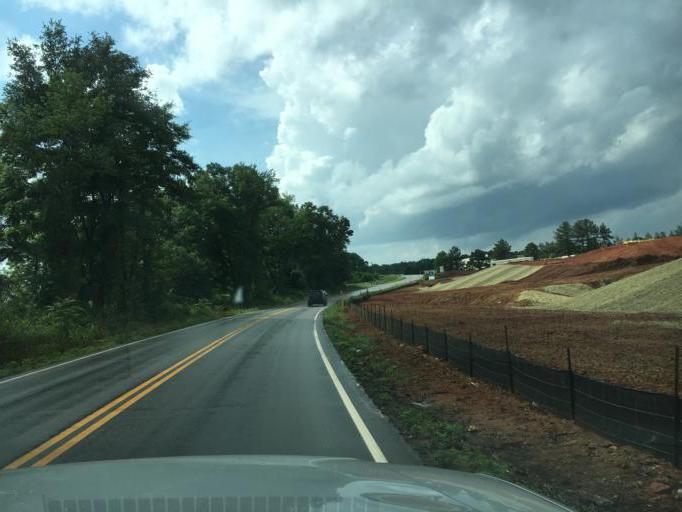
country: US
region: South Carolina
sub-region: Spartanburg County
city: Wellford
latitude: 34.9307
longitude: -82.0617
